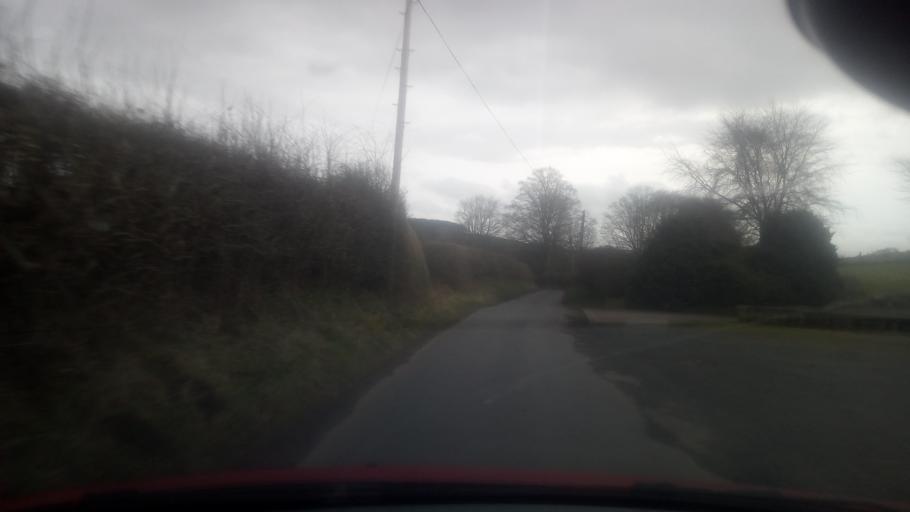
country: GB
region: Scotland
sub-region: The Scottish Borders
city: Jedburgh
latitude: 55.4753
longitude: -2.5403
